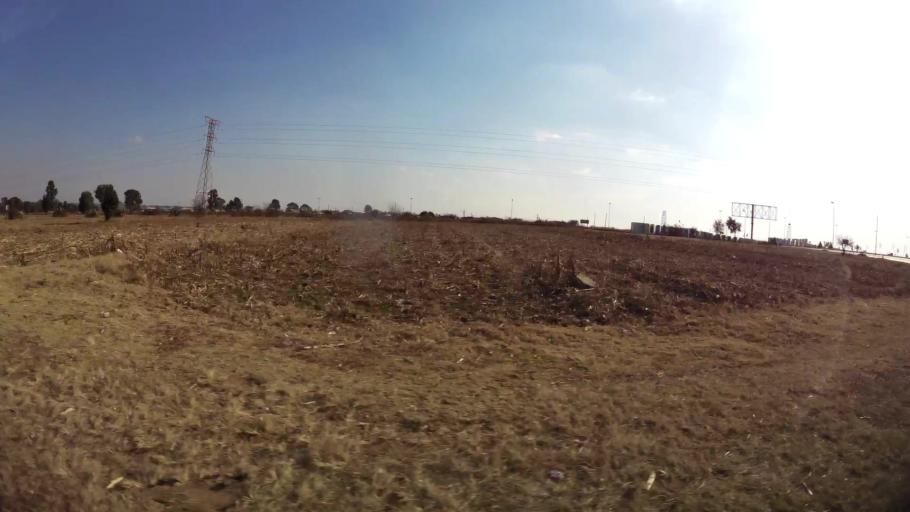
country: ZA
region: Gauteng
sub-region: Ekurhuleni Metropolitan Municipality
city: Brakpan
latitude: -26.1605
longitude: 28.3991
